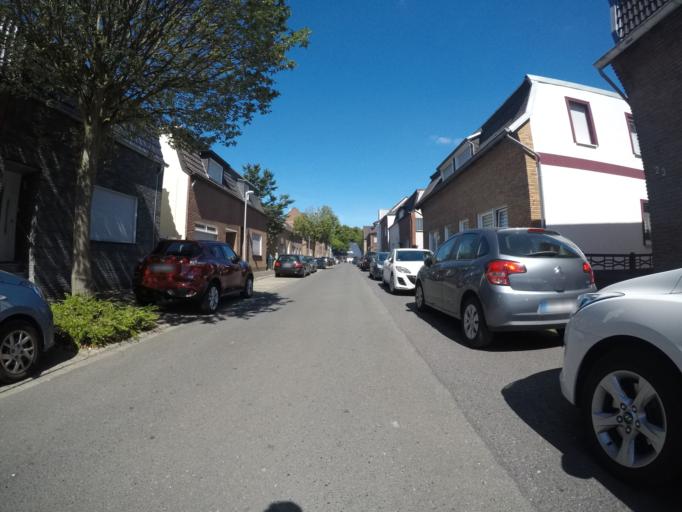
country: DE
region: North Rhine-Westphalia
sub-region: Regierungsbezirk Dusseldorf
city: Bocholt
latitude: 51.8324
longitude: 6.6051
